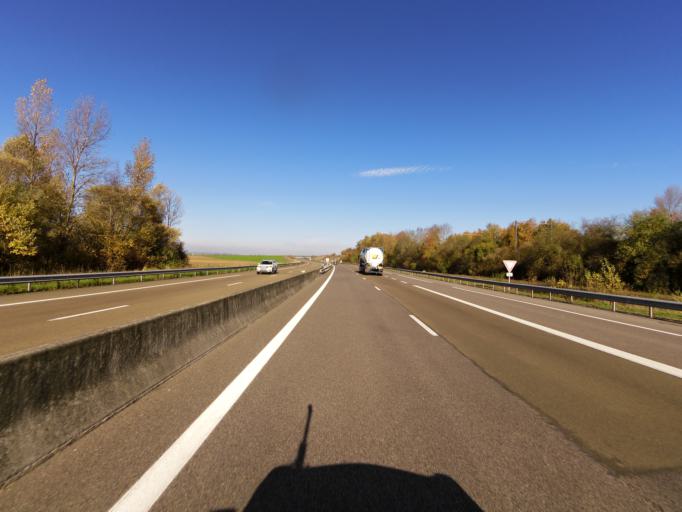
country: FR
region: Champagne-Ardenne
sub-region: Departement de la Marne
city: Fagnieres
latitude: 49.0094
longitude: 4.2979
